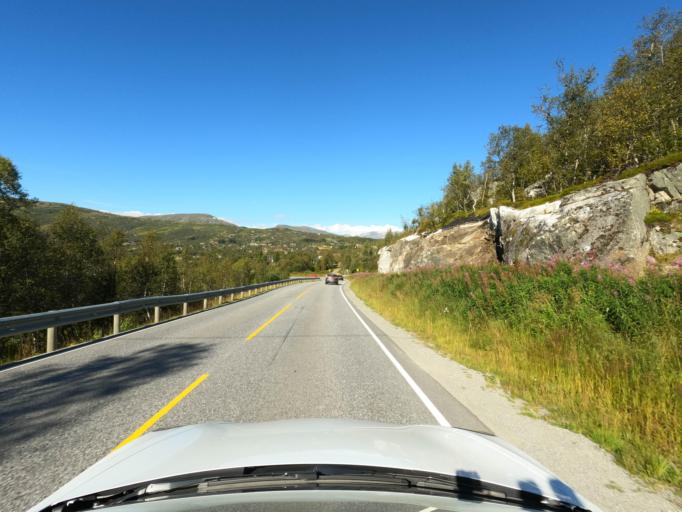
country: NO
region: Hordaland
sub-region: Eidfjord
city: Eidfjord
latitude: 60.4160
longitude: 7.2606
